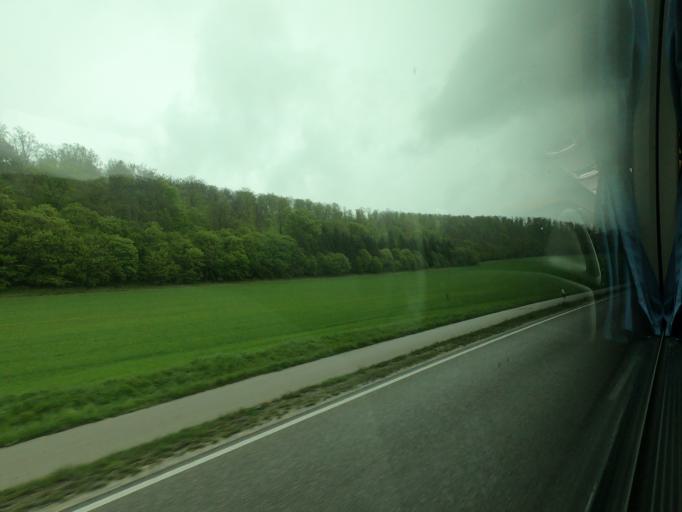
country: DE
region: Baden-Wuerttemberg
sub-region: Regierungsbezirk Stuttgart
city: Konigsbronn
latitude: 48.7343
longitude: 10.1474
